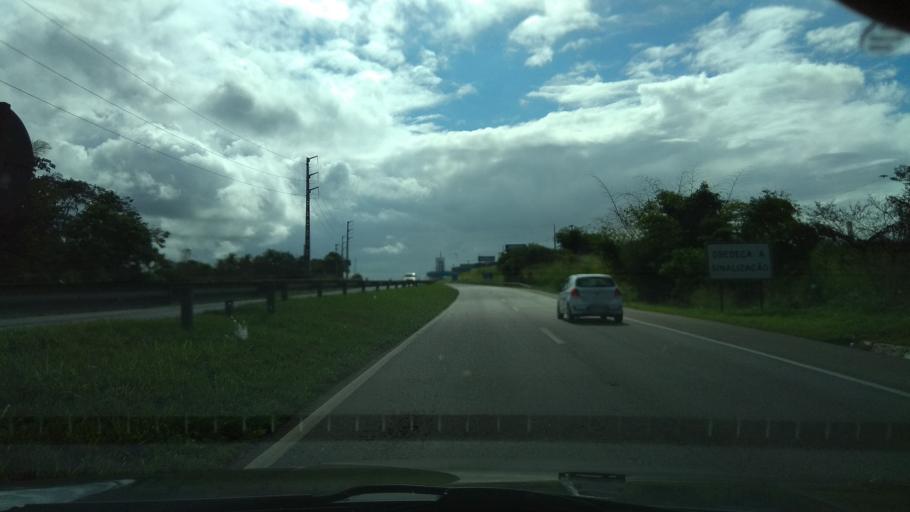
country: BR
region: Bahia
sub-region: Conceicao Do Jacuipe
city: Conceicao do Jacuipe
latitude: -12.3461
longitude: -38.8387
